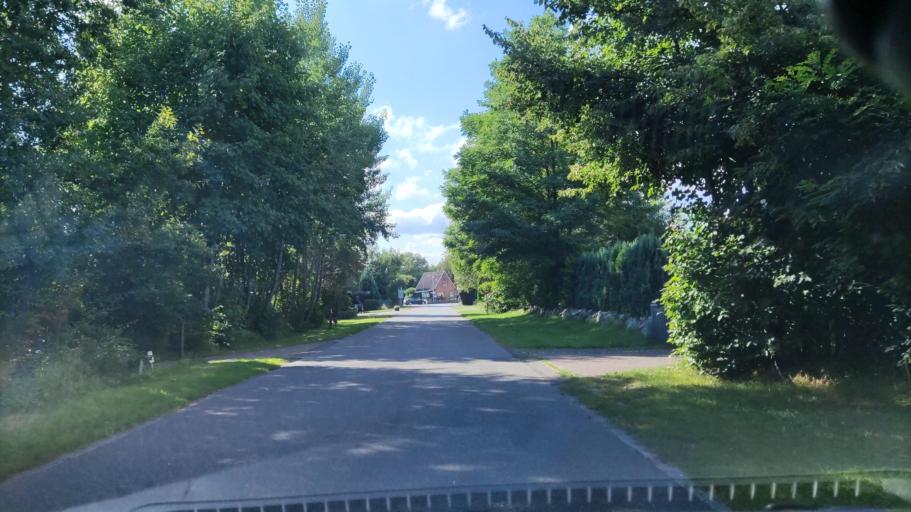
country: DE
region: Schleswig-Holstein
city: Luhnstedt
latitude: 54.2098
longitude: 9.7109
